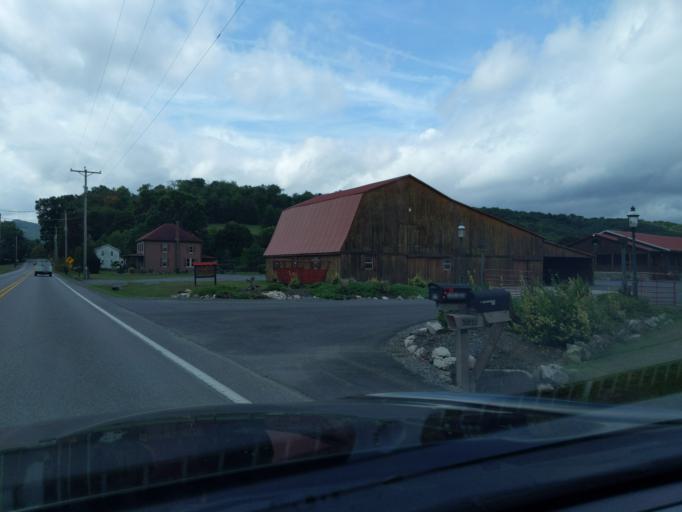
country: US
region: Pennsylvania
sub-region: Blair County
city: Duncansville
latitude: 40.3879
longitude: -78.4129
